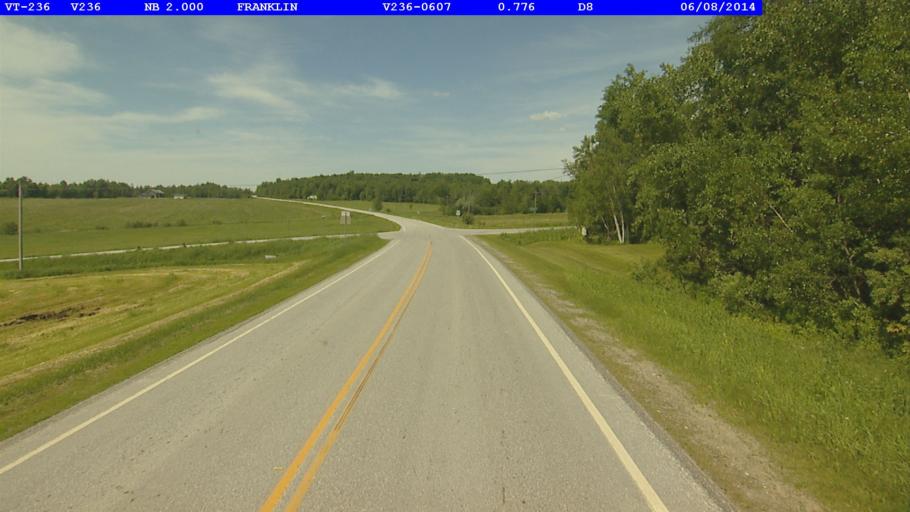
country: US
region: Vermont
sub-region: Franklin County
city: Enosburg Falls
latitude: 44.9393
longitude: -72.8624
